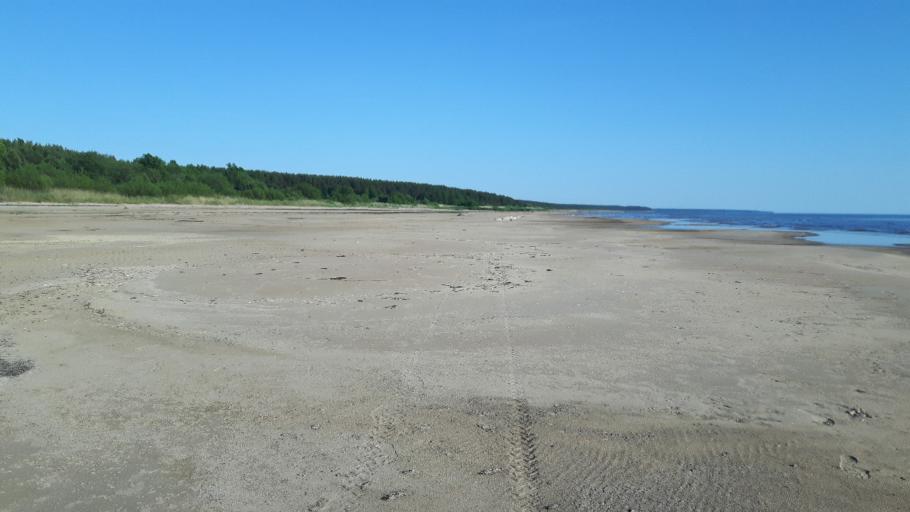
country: LV
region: Salacgrivas
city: Salacgriva
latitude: 57.6890
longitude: 24.3553
